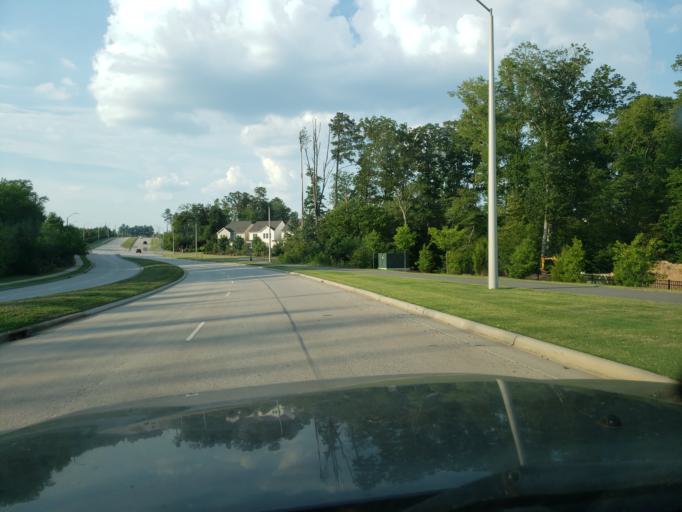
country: US
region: North Carolina
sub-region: Wake County
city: Green Level
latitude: 35.8378
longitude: -78.9110
